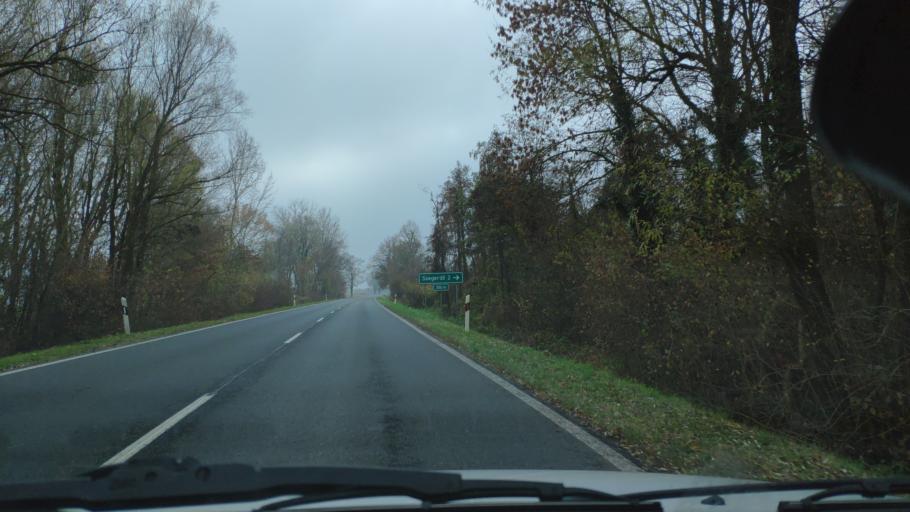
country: HU
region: Somogy
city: Balatonbereny
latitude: 46.6238
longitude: 17.2862
